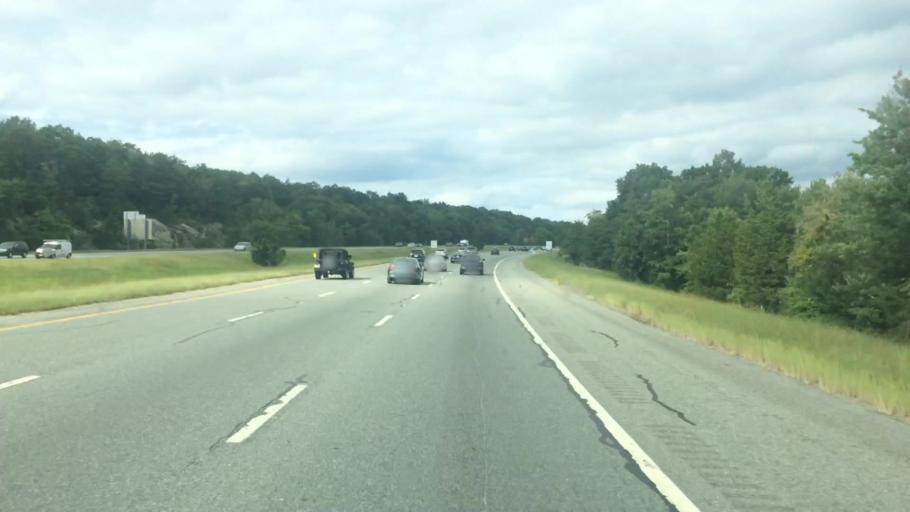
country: US
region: Rhode Island
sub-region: Providence County
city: Smithfield
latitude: 41.9256
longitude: -71.5043
